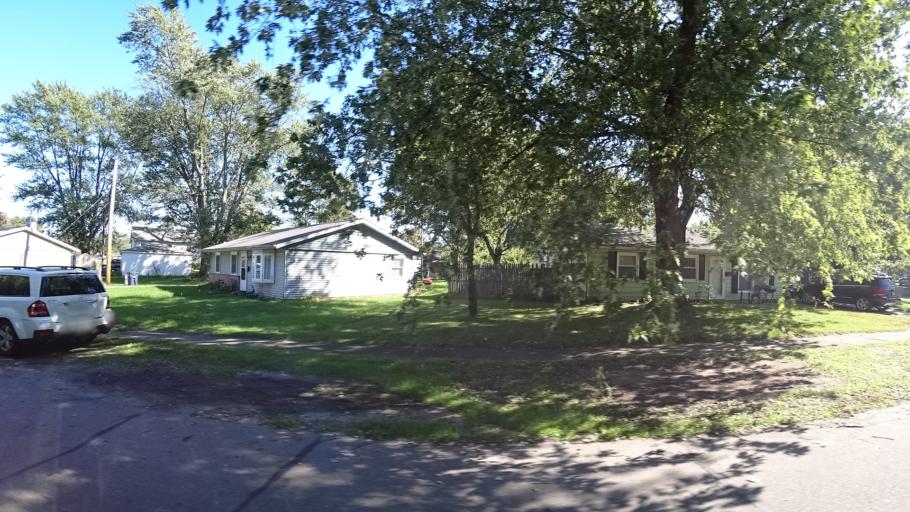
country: US
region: Indiana
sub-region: LaPorte County
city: Michigan City
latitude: 41.6965
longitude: -86.9093
